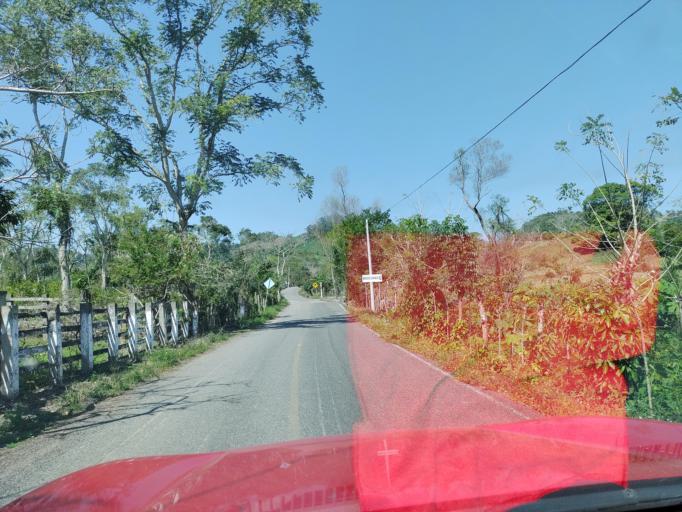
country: MX
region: Veracruz
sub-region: Papantla
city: Polutla
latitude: 20.4991
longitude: -97.2133
